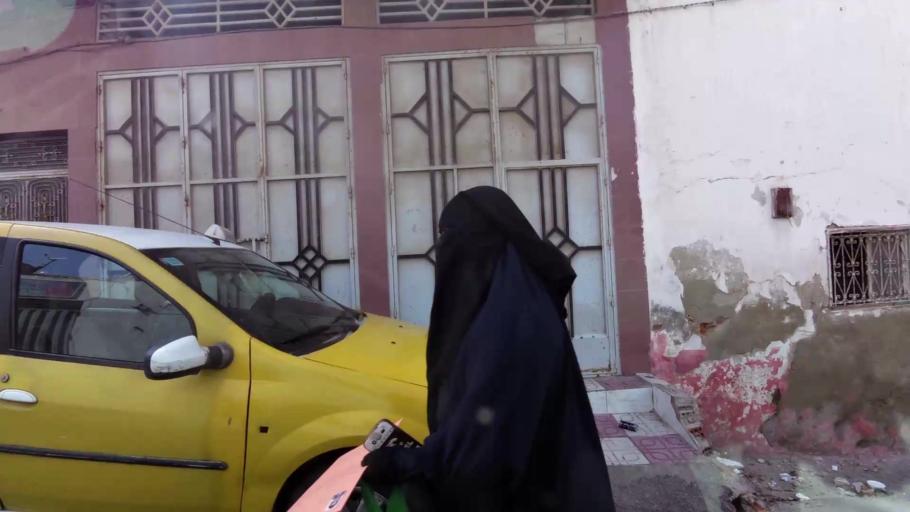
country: MA
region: Tanger-Tetouan
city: Tetouan
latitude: 35.5760
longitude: -5.3863
